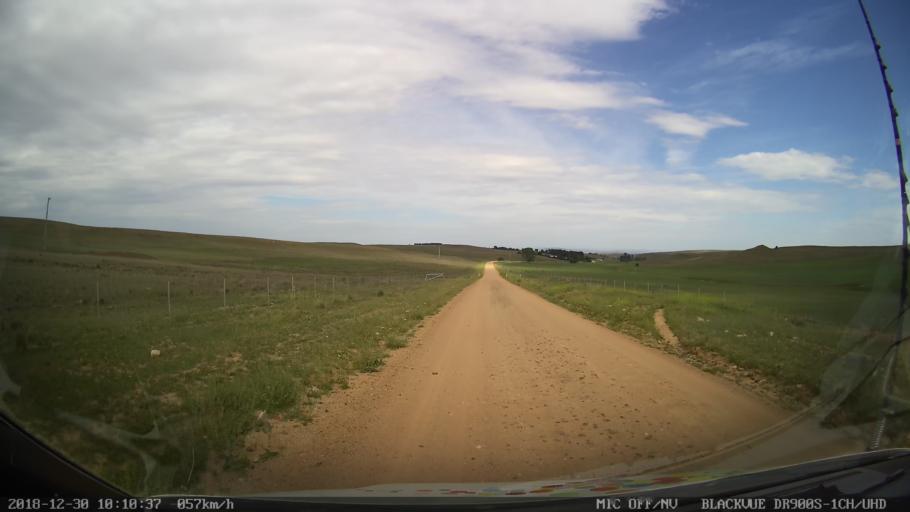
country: AU
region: New South Wales
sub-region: Cooma-Monaro
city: Cooma
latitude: -36.5504
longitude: 149.0930
